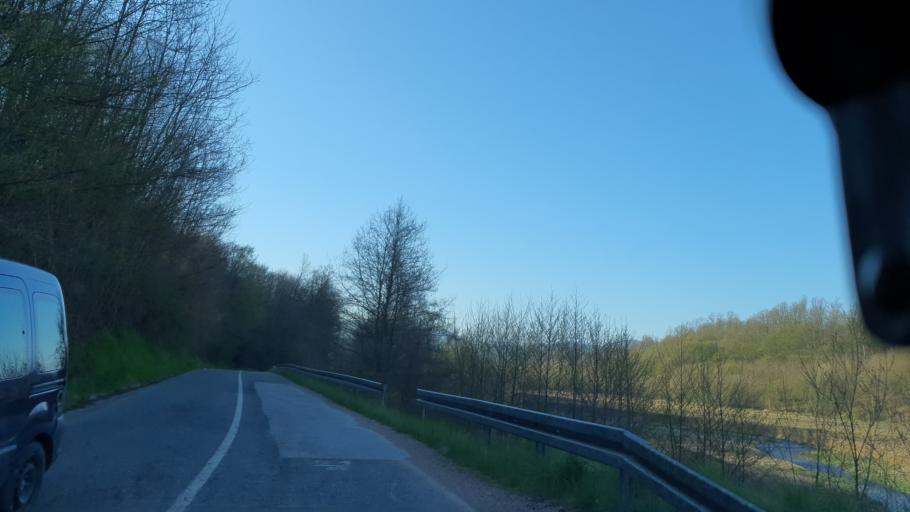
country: RS
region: Central Serbia
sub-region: Kolubarski Okrug
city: Osecina
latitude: 44.3404
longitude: 19.5212
